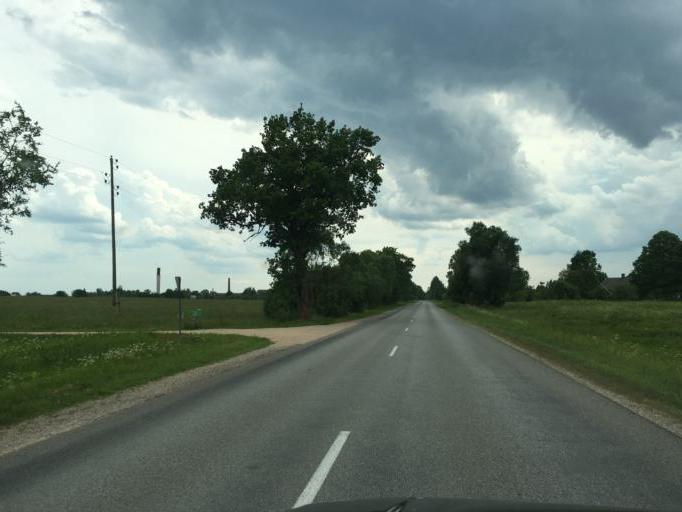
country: LV
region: Rugaju
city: Rugaji
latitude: 56.9145
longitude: 27.0686
